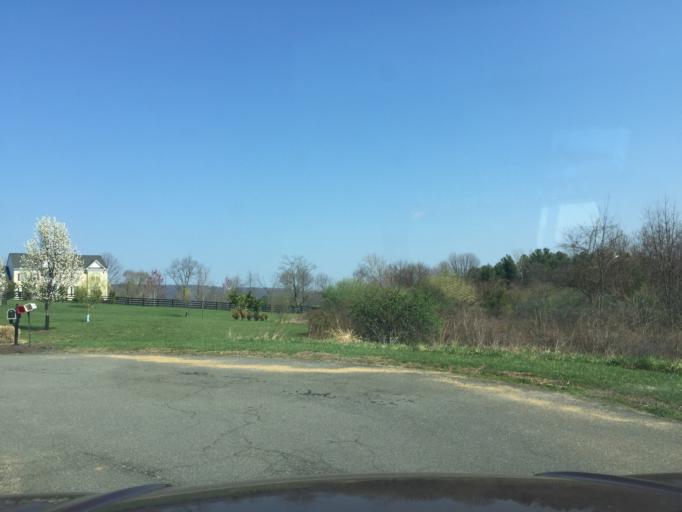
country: US
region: Maryland
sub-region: Frederick County
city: Brunswick
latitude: 39.2966
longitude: -77.5921
